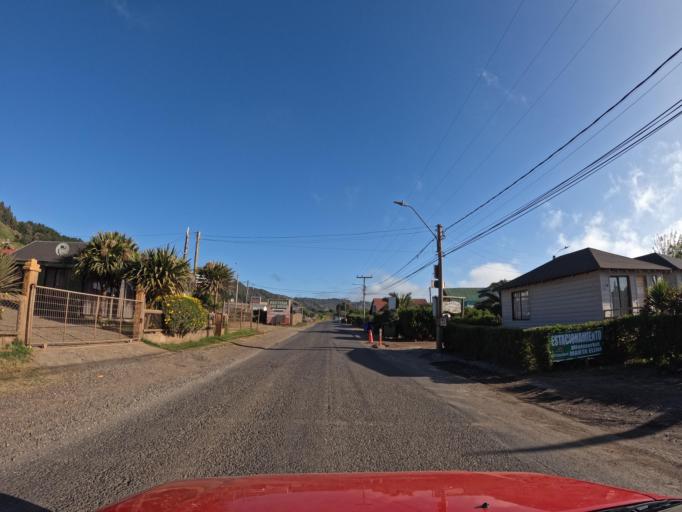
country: CL
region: Maule
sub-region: Provincia de Talca
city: Constitucion
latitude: -34.9252
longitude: -72.1794
